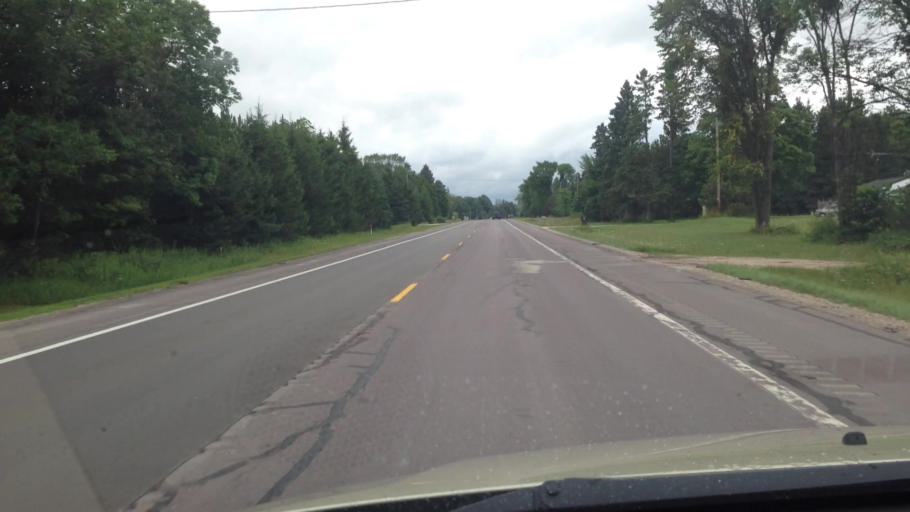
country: US
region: Michigan
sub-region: Schoolcraft County
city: Manistique
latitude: 46.0728
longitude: -85.9583
